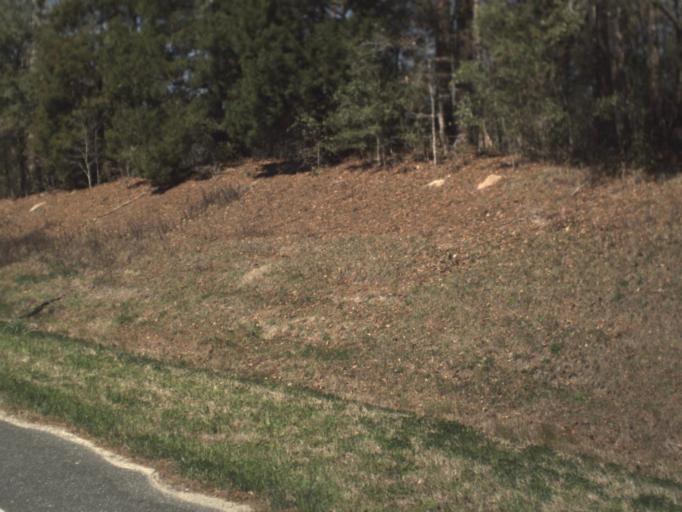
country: US
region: Florida
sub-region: Jackson County
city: Marianna
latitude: 30.7845
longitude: -85.2915
